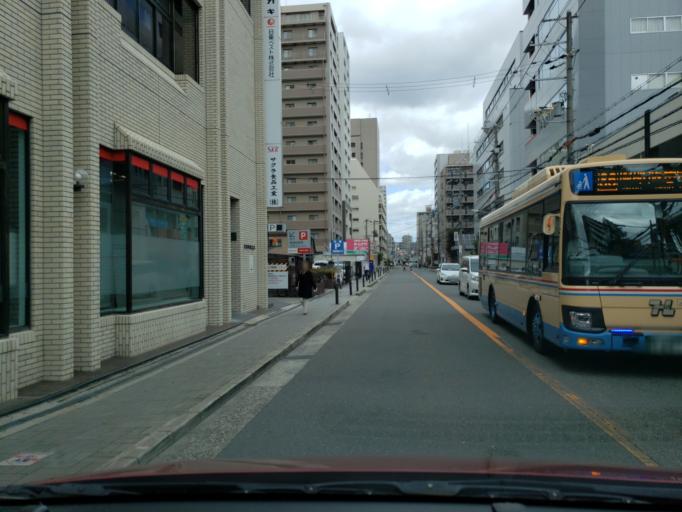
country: JP
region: Osaka
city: Suita
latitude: 34.7599
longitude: 135.4982
